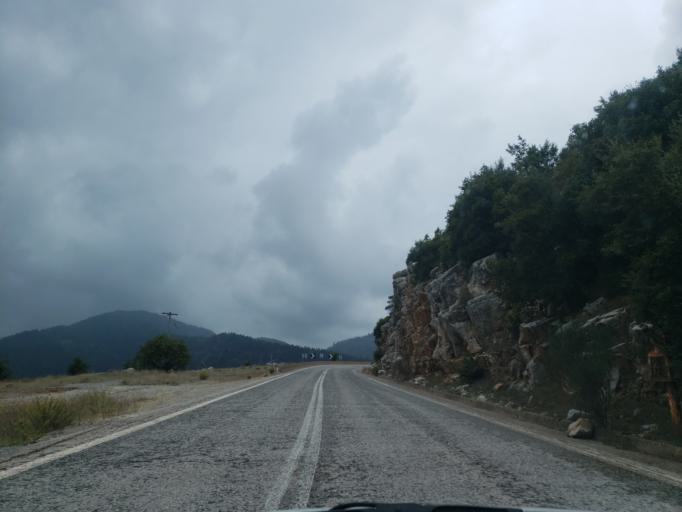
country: GR
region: Central Greece
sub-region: Nomos Fokidos
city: Amfissa
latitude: 38.6382
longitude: 22.3861
